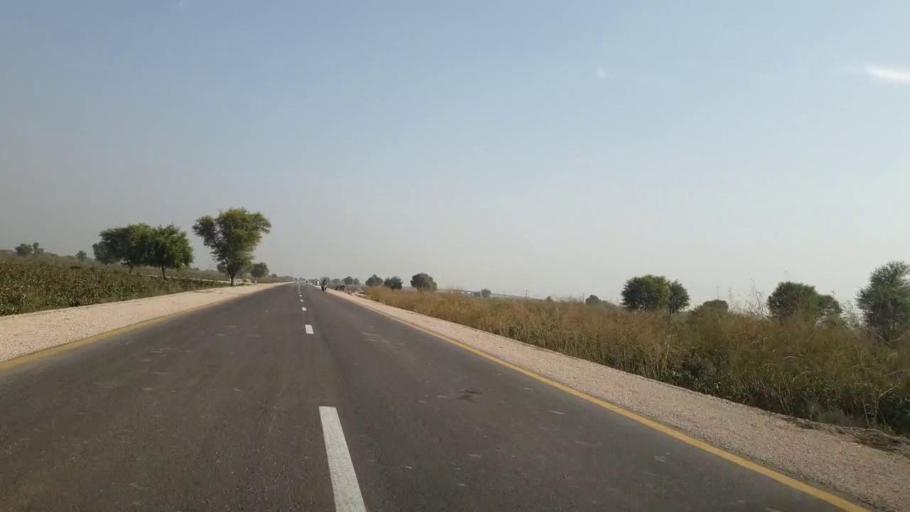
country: PK
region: Sindh
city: Sehwan
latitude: 26.4673
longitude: 67.7958
